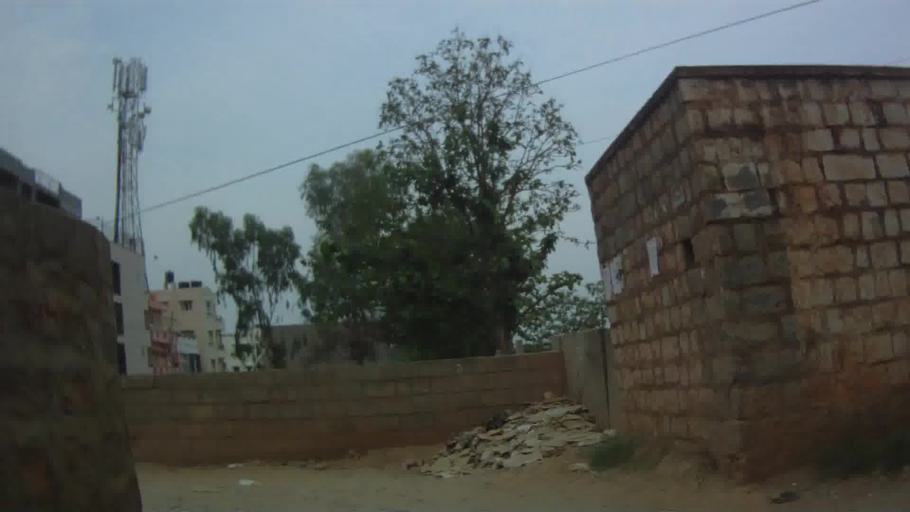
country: IN
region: Karnataka
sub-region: Bangalore Urban
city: Bangalore
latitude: 12.9621
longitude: 77.7058
